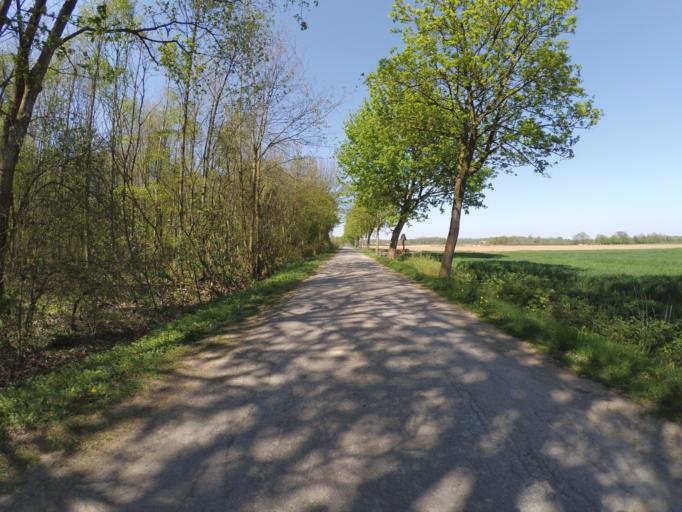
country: DE
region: North Rhine-Westphalia
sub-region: Regierungsbezirk Munster
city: Ascheberg
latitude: 51.8015
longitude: 7.6042
